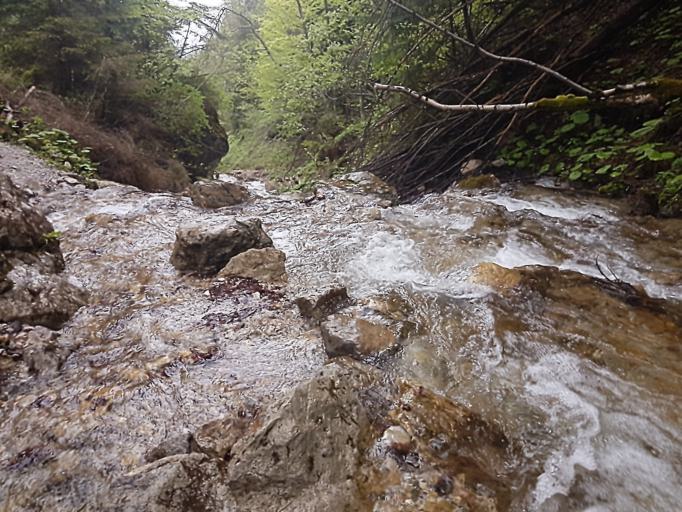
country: AT
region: Carinthia
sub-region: Politischer Bezirk Villach Land
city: Finkenstein am Faaker See
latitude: 46.5302
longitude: 13.9061
